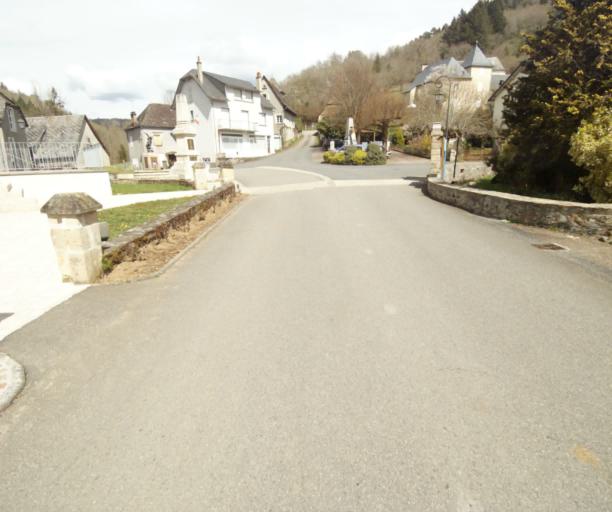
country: FR
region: Limousin
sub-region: Departement de la Correze
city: Argentat
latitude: 45.1757
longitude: 1.8755
